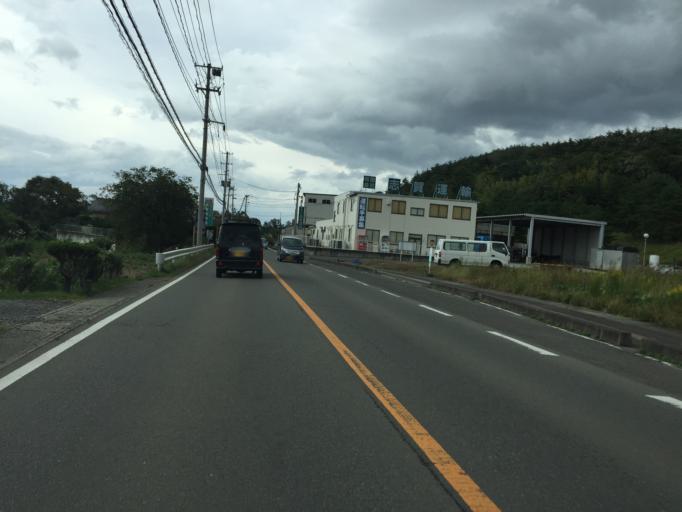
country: JP
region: Fukushima
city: Hobaramachi
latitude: 37.8074
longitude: 140.5330
